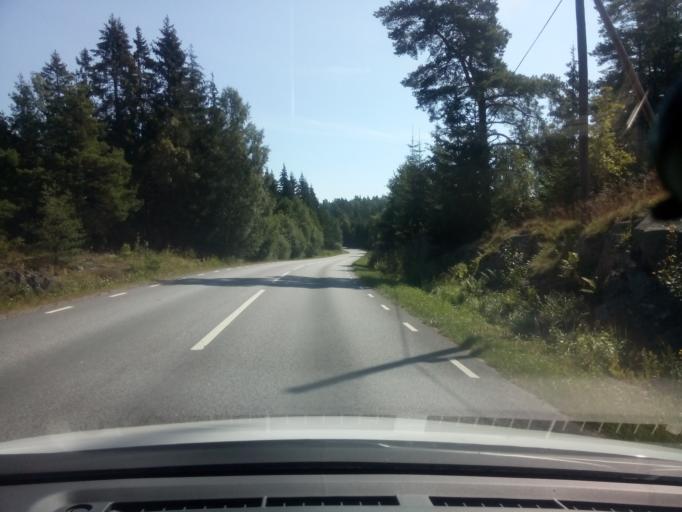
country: SE
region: Soedermanland
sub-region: Oxelosunds Kommun
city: Oxelosund
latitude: 58.7410
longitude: 17.1767
